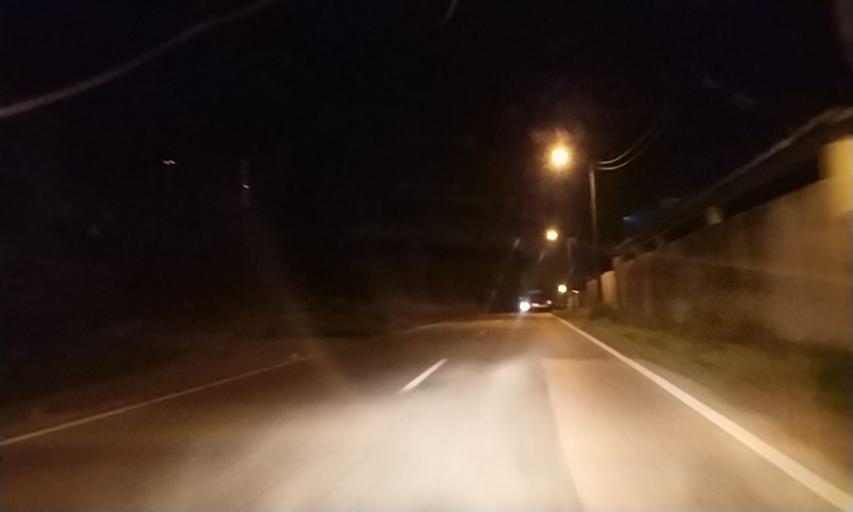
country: PT
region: Setubal
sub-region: Setubal
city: Setubal
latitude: 38.5109
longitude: -8.8546
